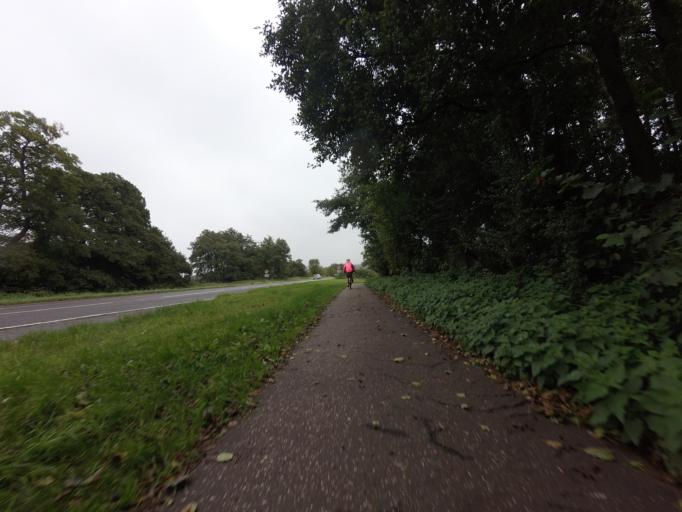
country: GB
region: England
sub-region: Norfolk
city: Dersingham
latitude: 52.8085
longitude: 0.4848
